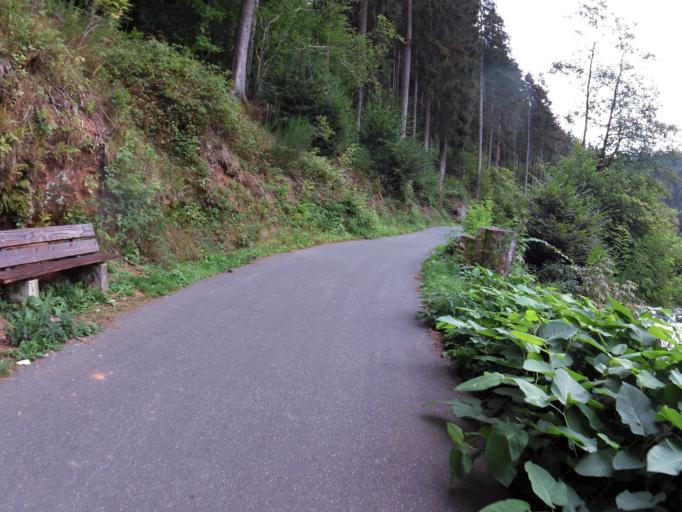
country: DE
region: Rheinland-Pfalz
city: Sankt Thomas
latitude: 50.0561
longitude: 6.6024
